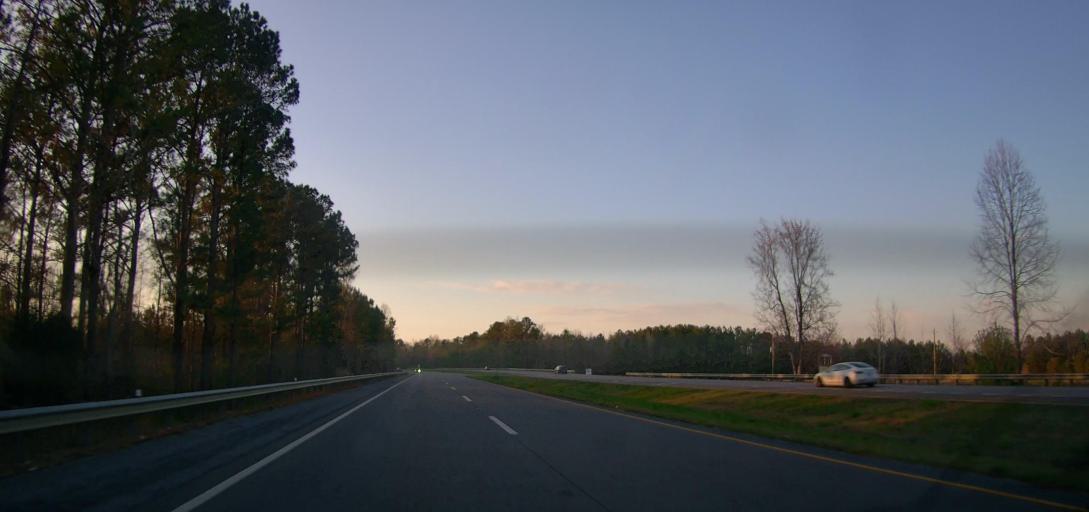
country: US
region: Alabama
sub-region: Talladega County
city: Sylacauga
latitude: 33.1360
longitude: -86.2484
